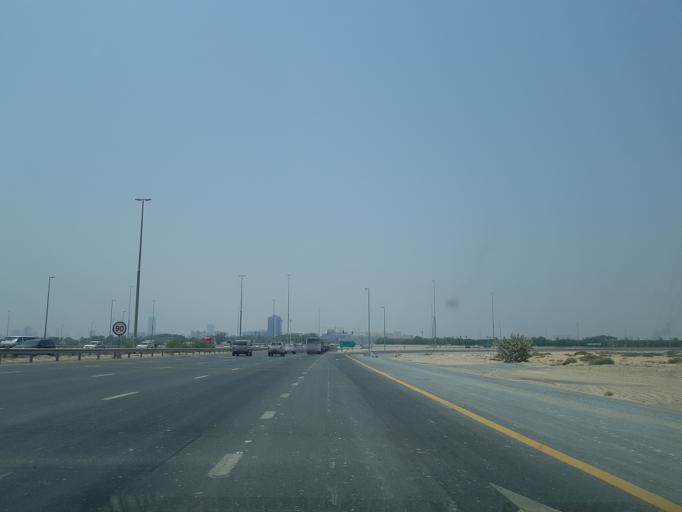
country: AE
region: Dubai
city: Dubai
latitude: 25.0334
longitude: 55.2625
